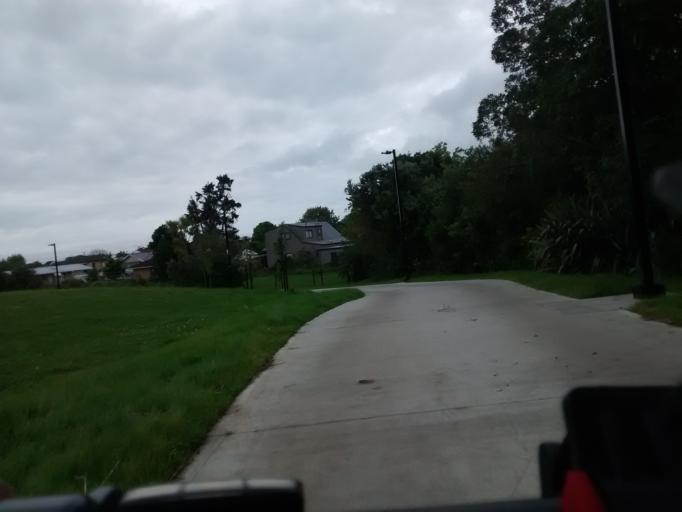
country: NZ
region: Auckland
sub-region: Auckland
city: Rosebank
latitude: -36.8898
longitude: 174.7065
